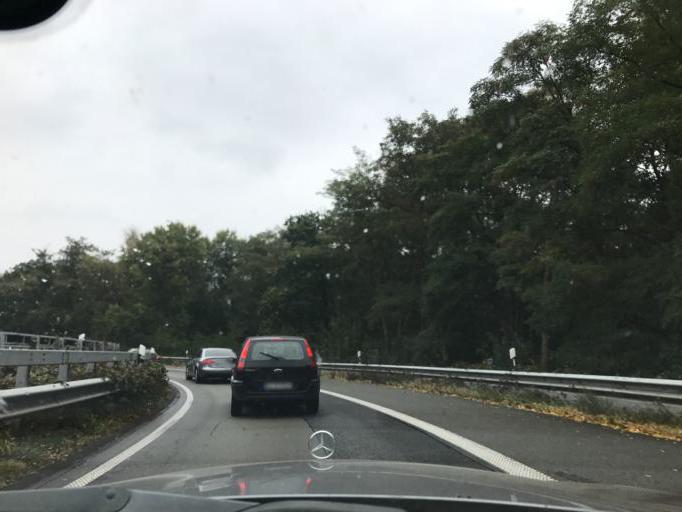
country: DE
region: Lower Saxony
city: Oldenburg
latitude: 53.1522
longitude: 8.1953
